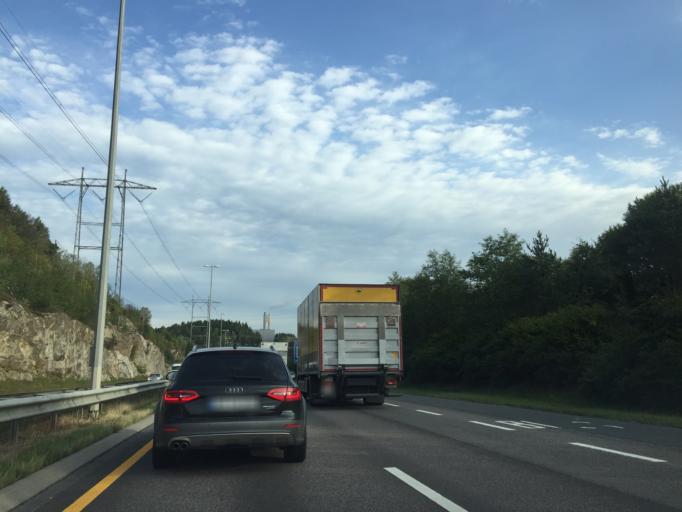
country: NO
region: Akershus
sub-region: Oppegard
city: Kolbotn
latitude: 59.8303
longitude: 10.8424
